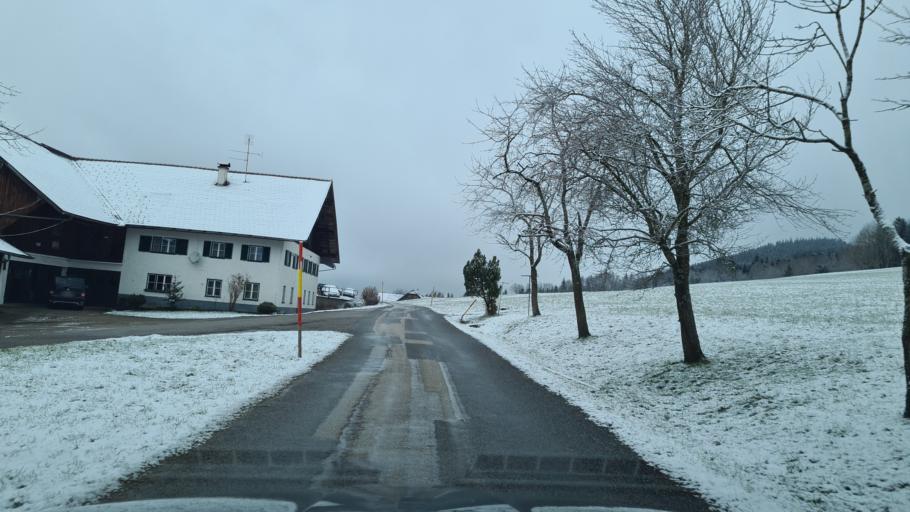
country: AT
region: Upper Austria
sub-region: Politischer Bezirk Vocklabruck
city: Oberhofen am Irrsee
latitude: 47.9409
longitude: 13.3226
